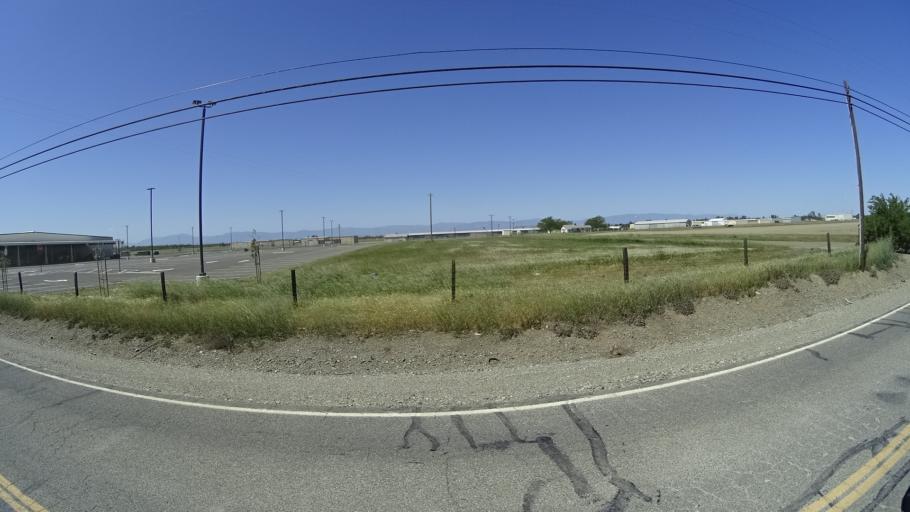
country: US
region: California
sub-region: Glenn County
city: Orland
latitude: 39.7205
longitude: -122.1414
